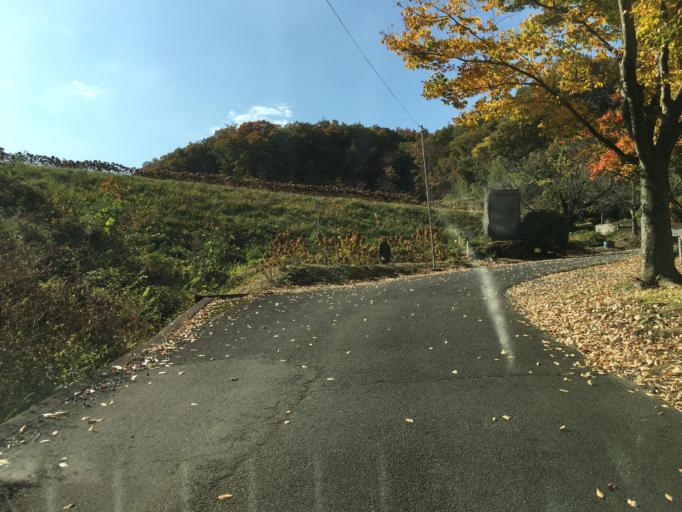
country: JP
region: Fukushima
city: Fukushima-shi
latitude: 37.7017
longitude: 140.4339
